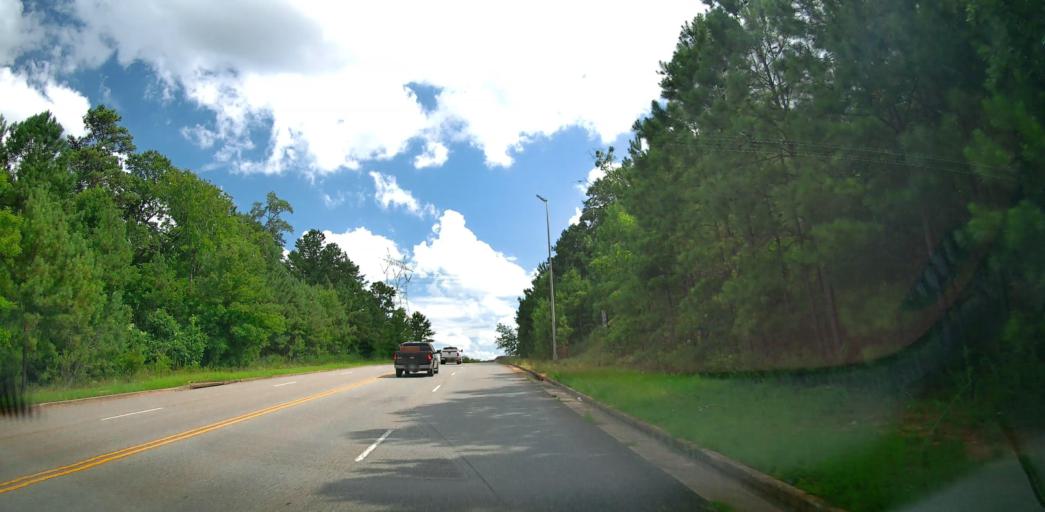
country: US
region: Georgia
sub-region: Houston County
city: Centerville
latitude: 32.5898
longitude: -83.6556
